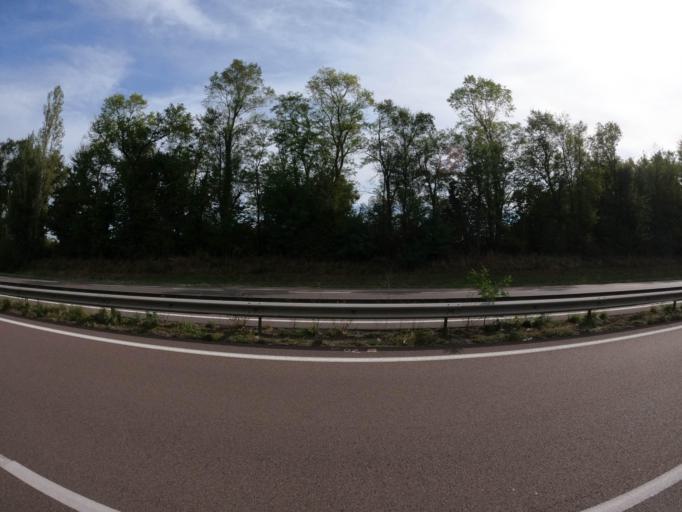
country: FR
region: Bourgogne
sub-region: Departement de Saone-et-Loire
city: Sanvignes-les-Mines
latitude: 46.6473
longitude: 4.3293
